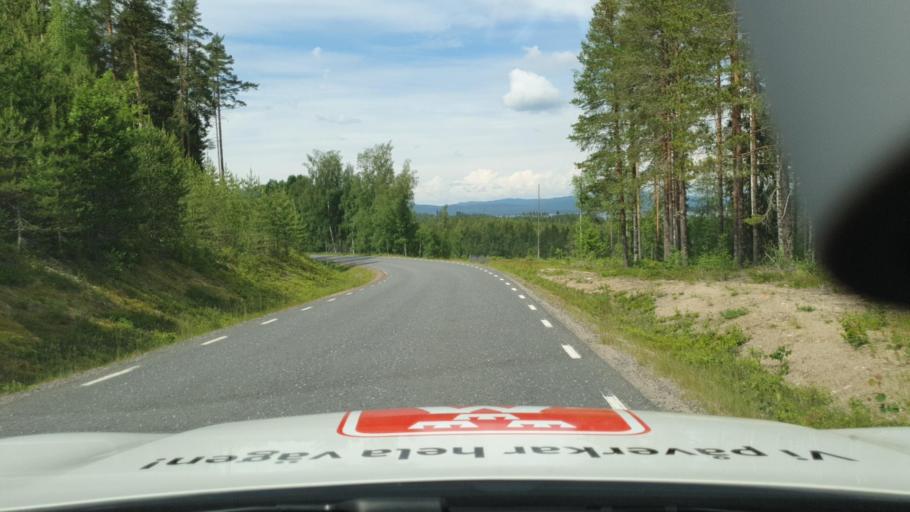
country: SE
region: Vaermland
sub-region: Torsby Kommun
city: Torsby
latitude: 60.6697
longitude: 12.6942
